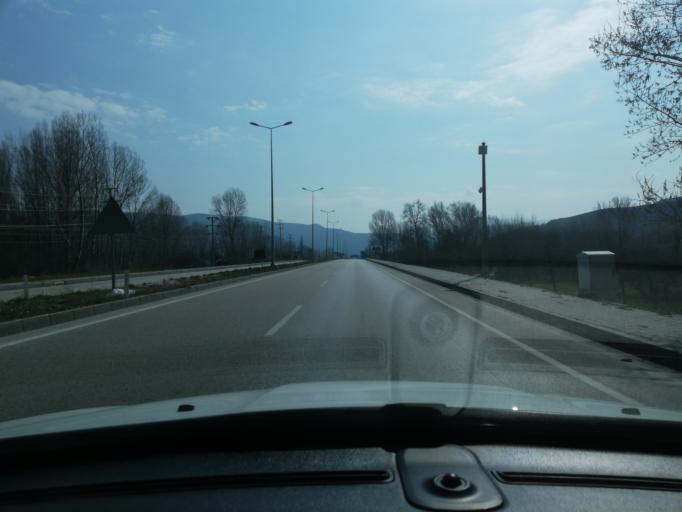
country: TR
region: Cankiri
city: Ilgaz
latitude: 40.9078
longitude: 33.6371
